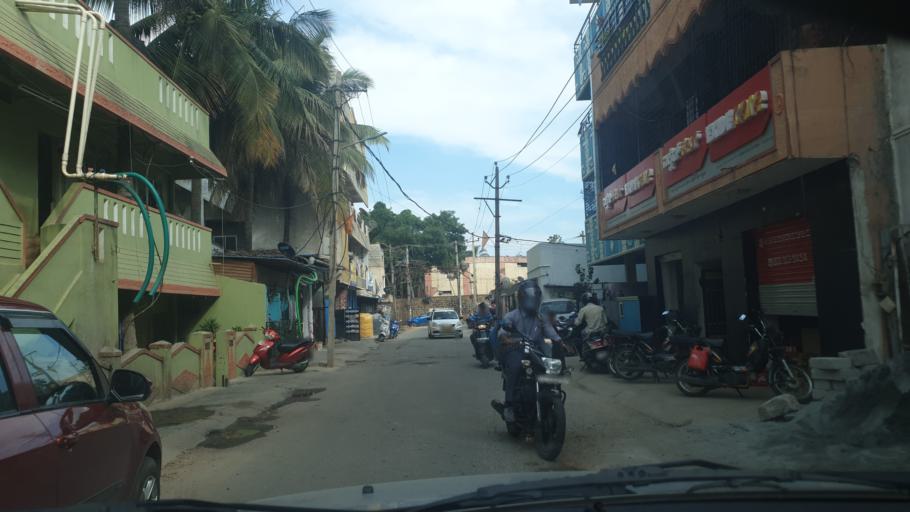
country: IN
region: Karnataka
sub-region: Bangalore Urban
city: Bangalore
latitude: 12.9642
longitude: 77.6815
